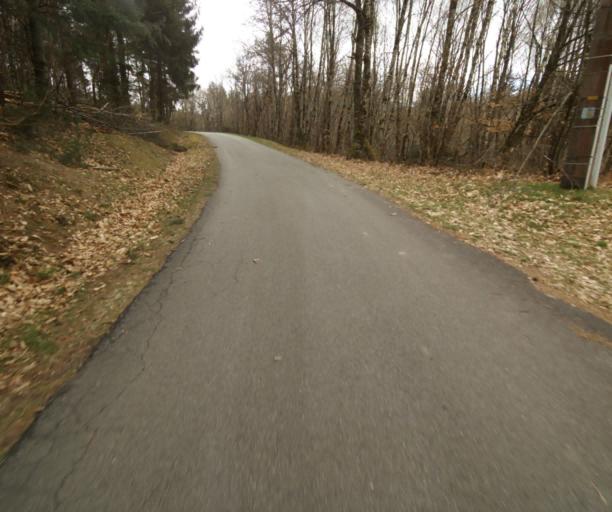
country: FR
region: Limousin
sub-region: Departement de la Correze
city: Correze
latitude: 45.3239
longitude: 1.9413
